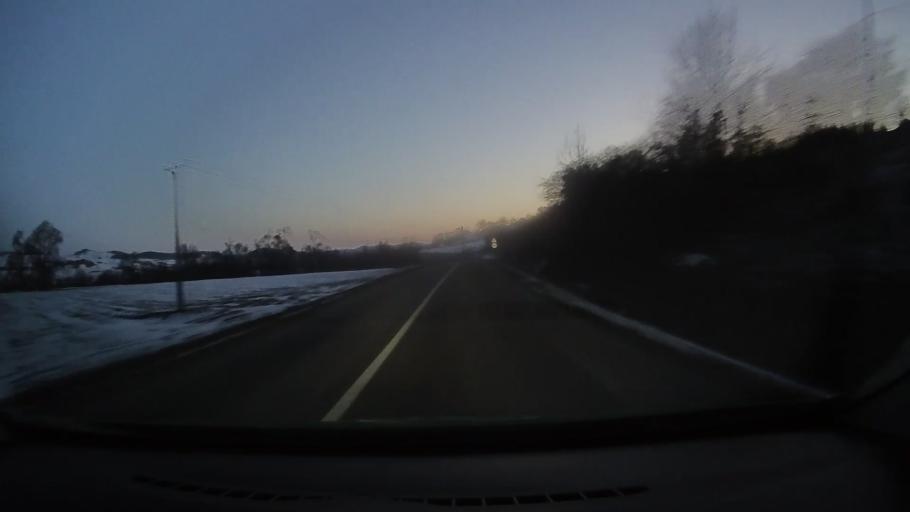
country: RO
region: Sibiu
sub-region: Comuna Alma
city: Alma
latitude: 46.1988
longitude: 24.4452
